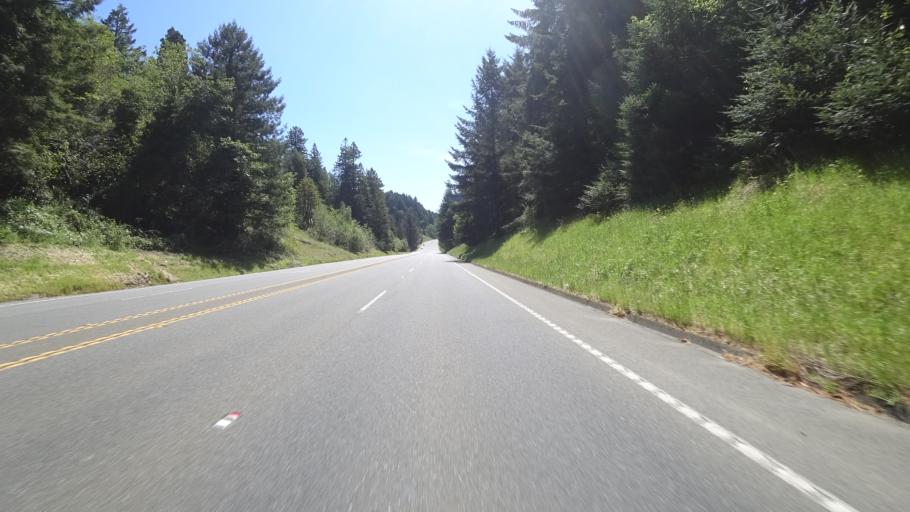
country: US
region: California
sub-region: Humboldt County
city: Westhaven-Moonstone
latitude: 41.0472
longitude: -124.1192
